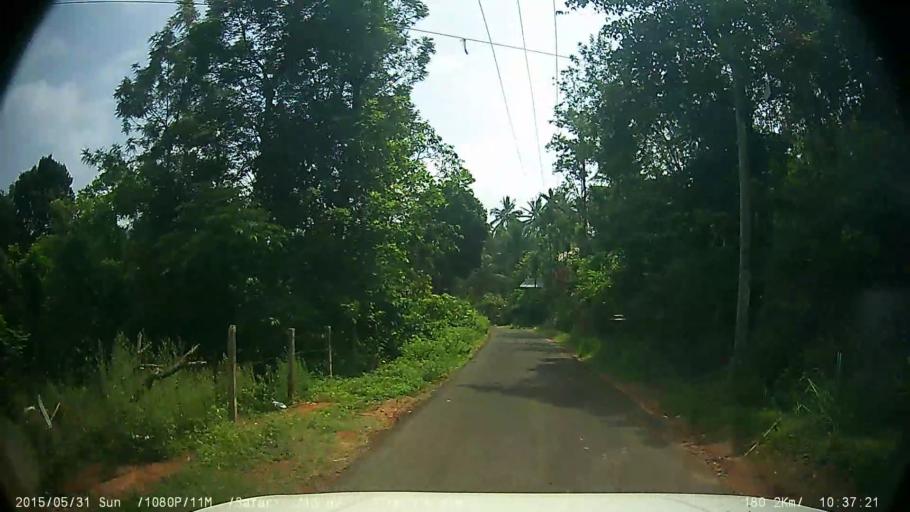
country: IN
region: Kerala
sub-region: Wayanad
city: Kalpetta
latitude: 11.5071
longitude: 76.1507
